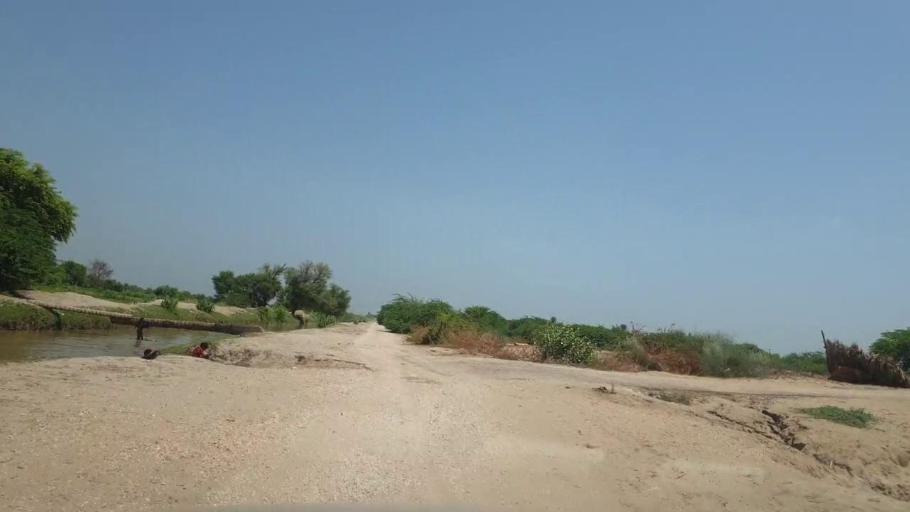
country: PK
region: Sindh
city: Rohri
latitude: 27.6308
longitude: 69.0993
